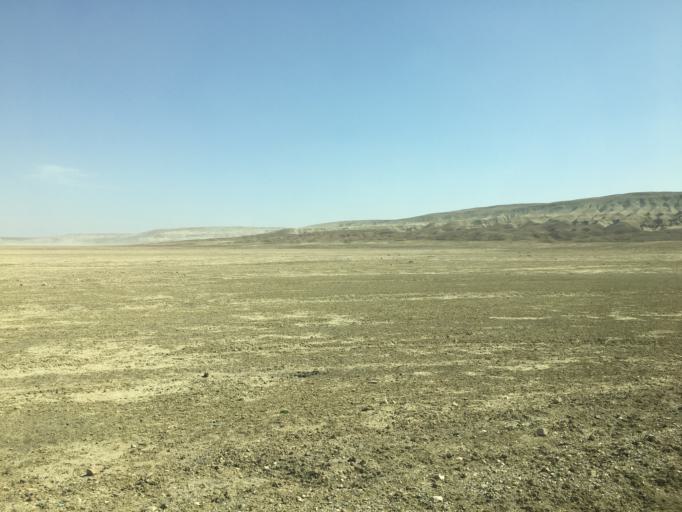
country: TM
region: Balkan
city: Balkanabat
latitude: 40.3669
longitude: 54.3905
